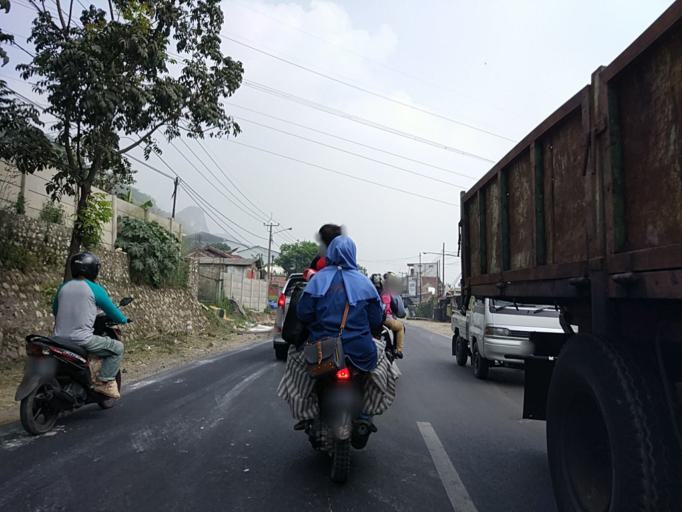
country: ID
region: West Java
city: Padalarang
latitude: -6.8324
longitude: 107.4637
